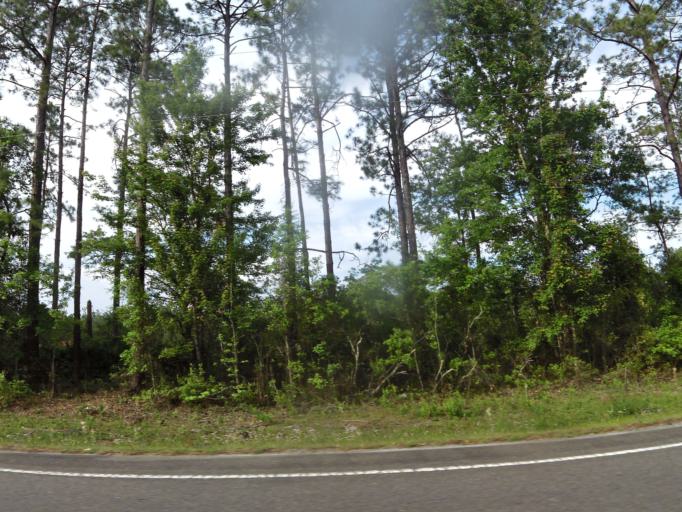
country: US
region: Florida
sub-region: Nassau County
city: Yulee
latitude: 30.6924
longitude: -81.6816
